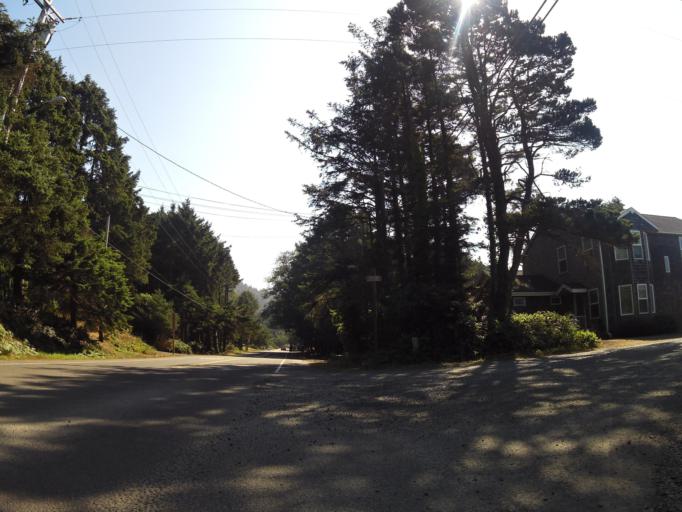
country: US
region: Oregon
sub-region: Clatsop County
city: Cannon Beach
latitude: 45.8674
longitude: -123.9598
